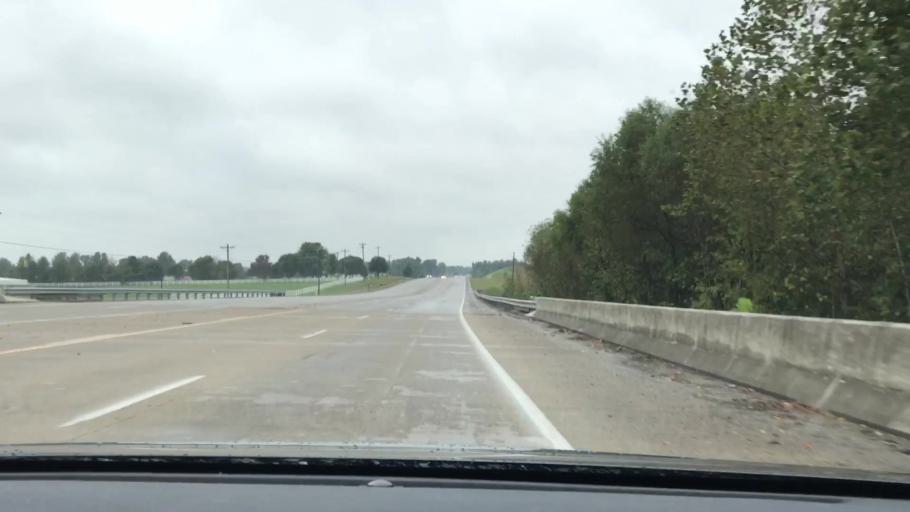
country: US
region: Kentucky
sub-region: Hopkins County
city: Madisonville
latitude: 37.3339
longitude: -87.4211
